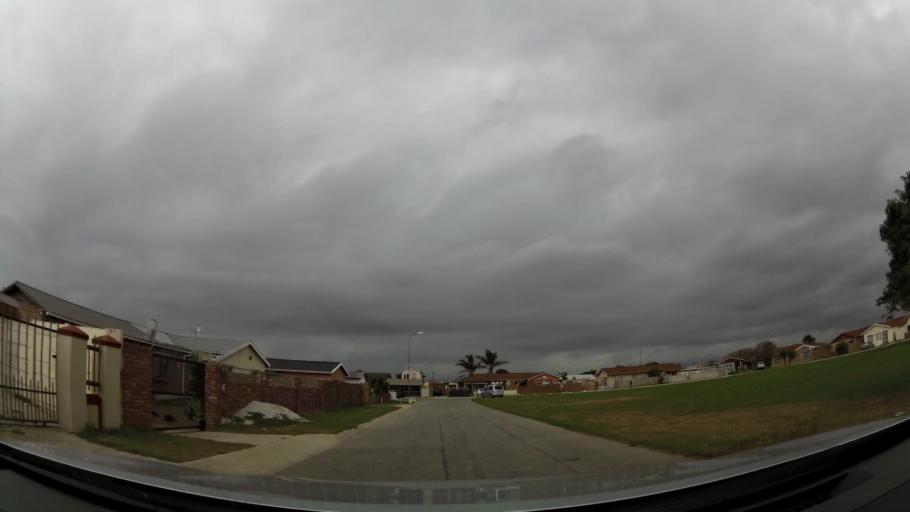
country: ZA
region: Eastern Cape
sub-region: Nelson Mandela Bay Metropolitan Municipality
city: Port Elizabeth
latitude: -33.8970
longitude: 25.5641
